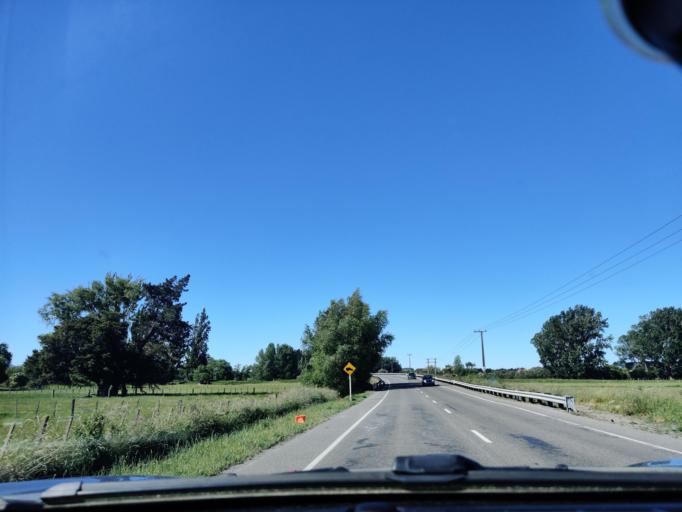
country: NZ
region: Wellington
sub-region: Masterton District
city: Masterton
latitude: -41.0612
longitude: 175.4923
